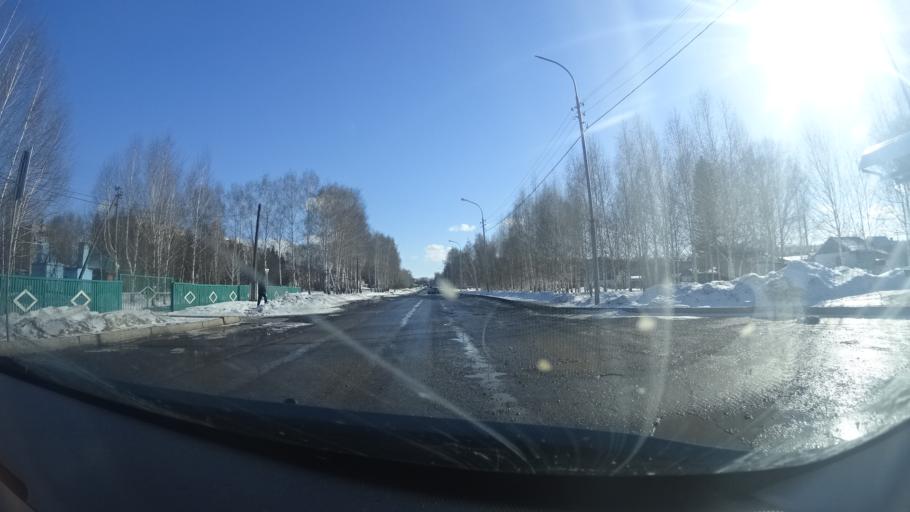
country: RU
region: Bashkortostan
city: Chishmy
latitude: 54.5903
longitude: 55.3688
